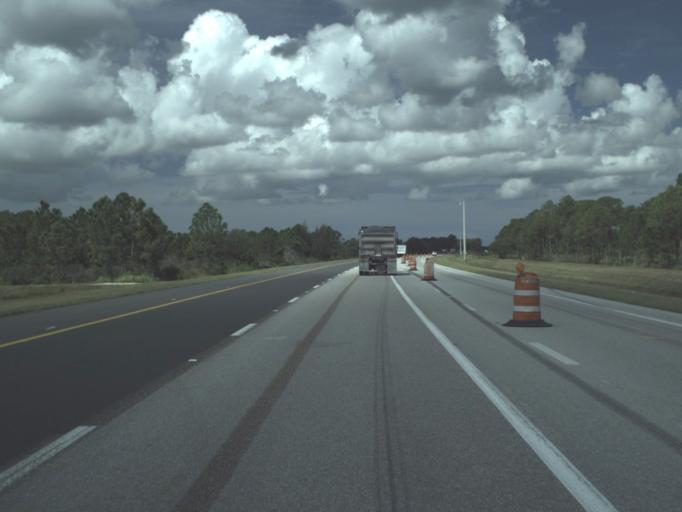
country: US
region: Florida
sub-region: Sarasota County
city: Warm Mineral Springs
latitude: 27.1010
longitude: -82.2830
